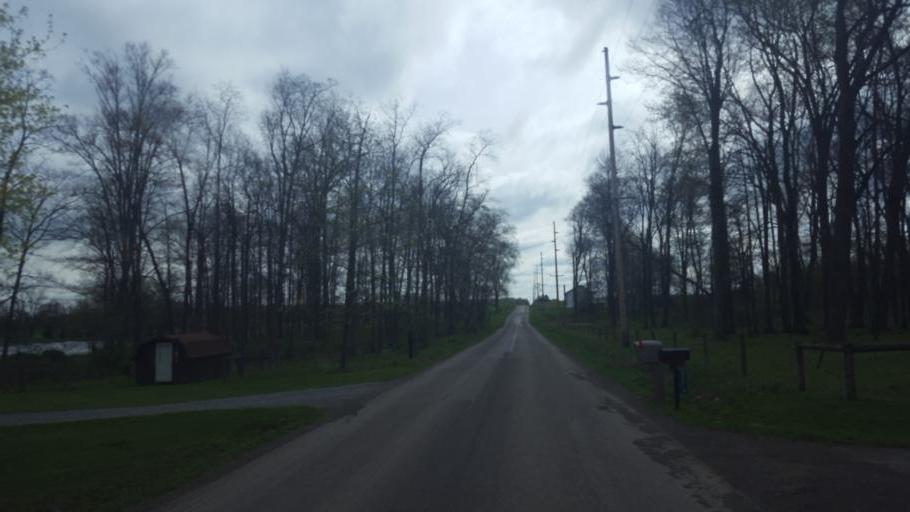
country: US
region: Ohio
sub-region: Wayne County
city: Apple Creek
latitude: 40.7118
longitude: -81.8259
